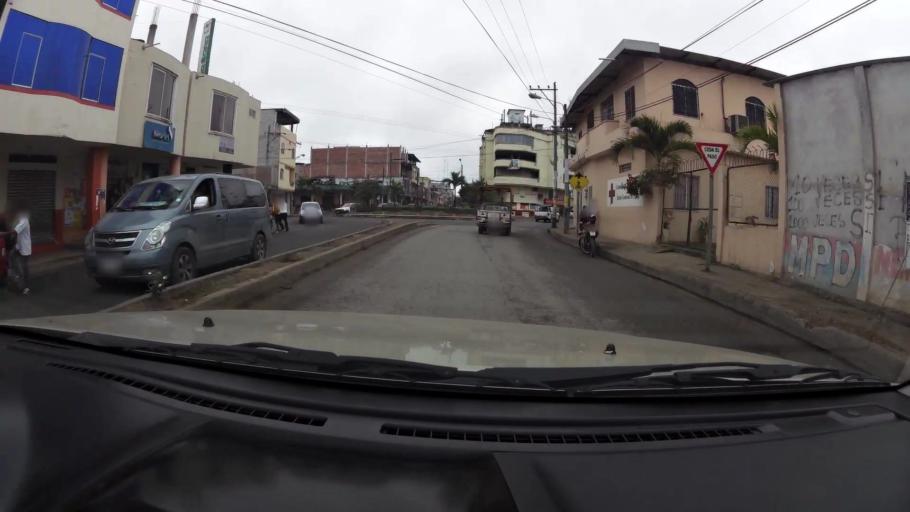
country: EC
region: El Oro
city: Pasaje
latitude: -3.3300
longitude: -79.8113
